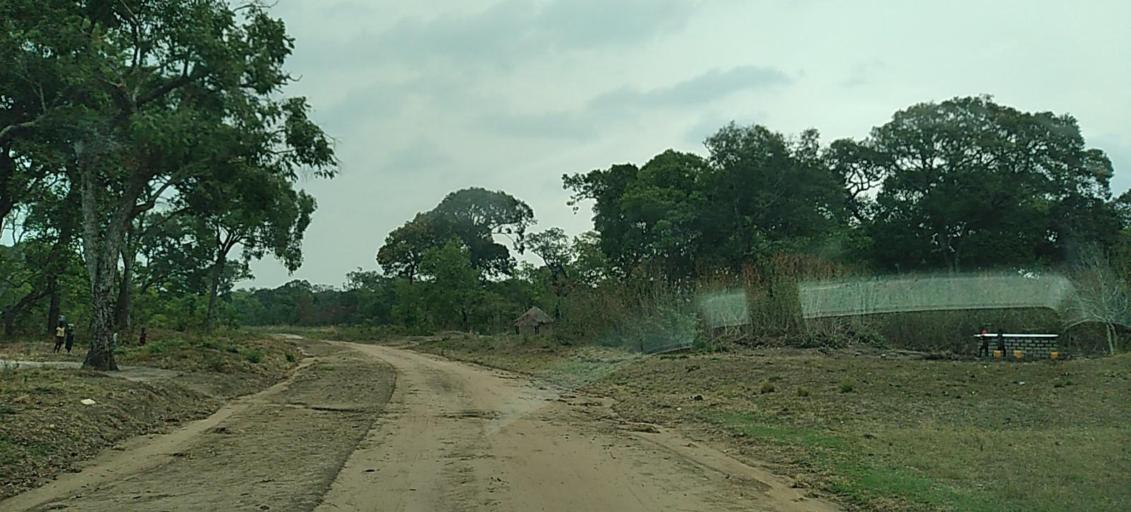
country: ZM
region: North-Western
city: Mwinilunga
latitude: -11.4212
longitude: 24.5960
